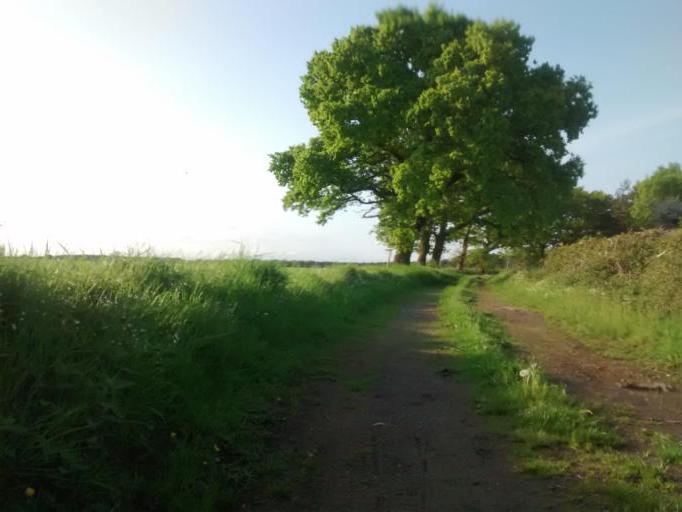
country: GB
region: England
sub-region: County Durham
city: West Cornforth
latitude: 54.7303
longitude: -1.5480
